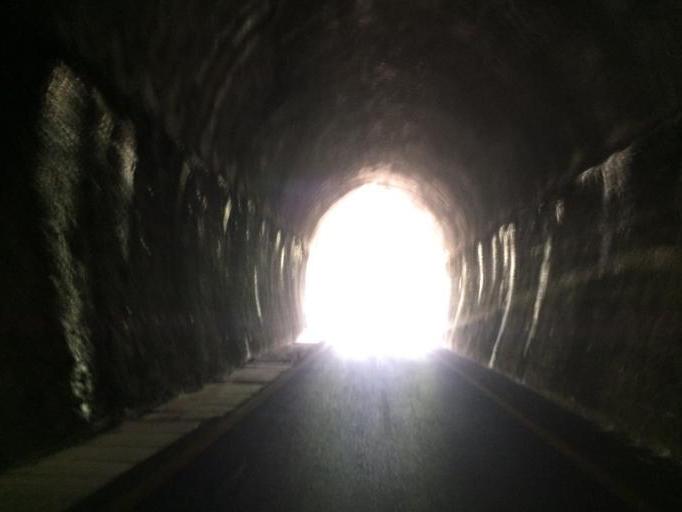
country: IT
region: Friuli Venezia Giulia
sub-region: Provincia di Udine
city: Dogna
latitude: 46.4565
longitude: 13.3100
